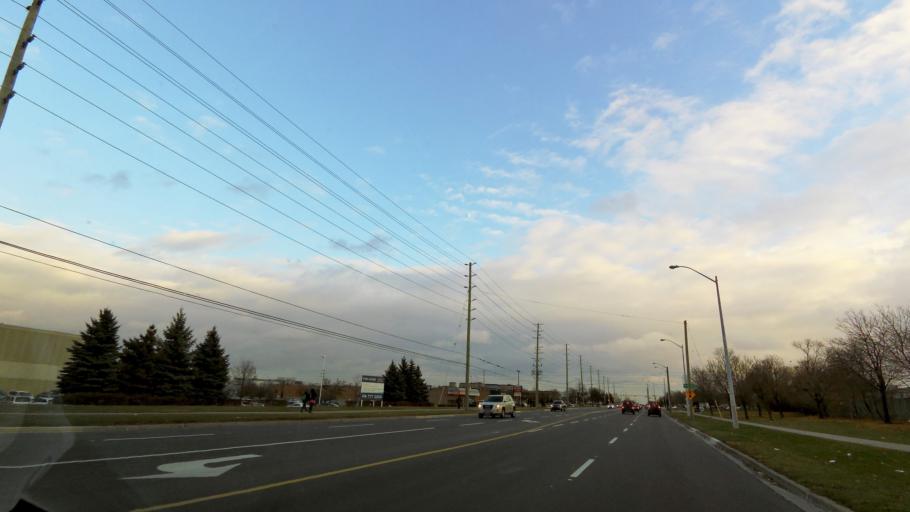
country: CA
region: Ontario
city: Brampton
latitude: 43.7358
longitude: -79.7093
